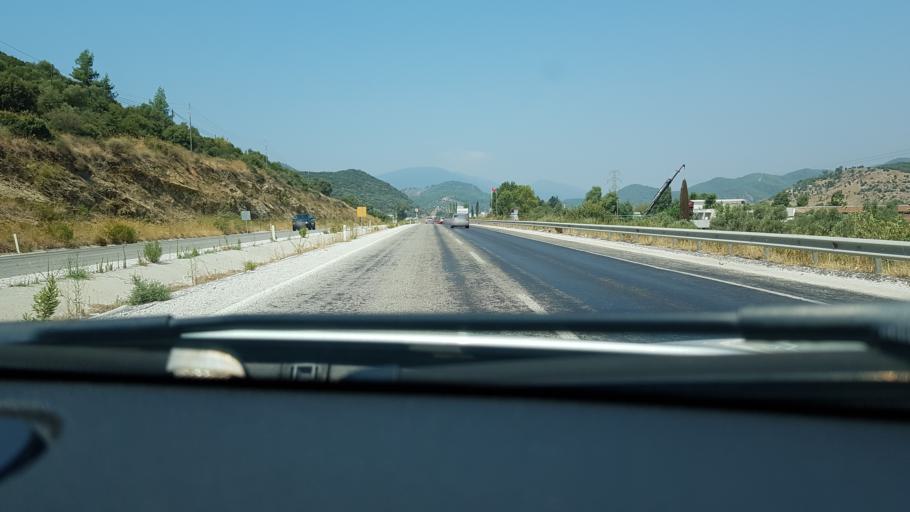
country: TR
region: Mugla
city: Milas
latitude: 37.3390
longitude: 27.7491
